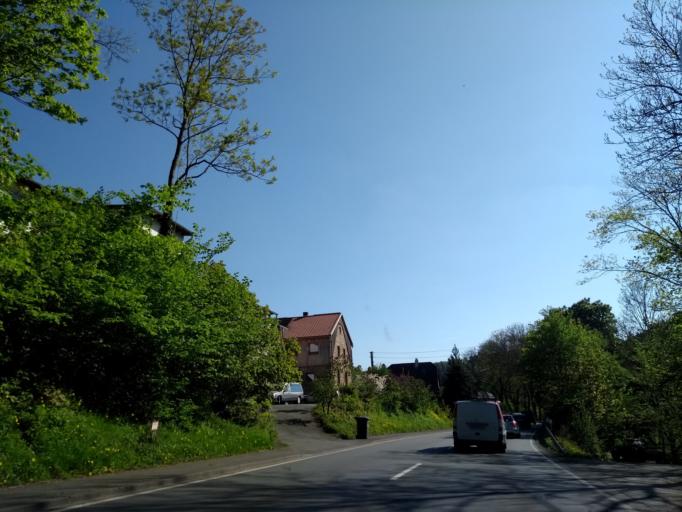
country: DE
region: Hesse
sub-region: Regierungsbezirk Kassel
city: Korbach
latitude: 51.2325
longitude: 8.8947
